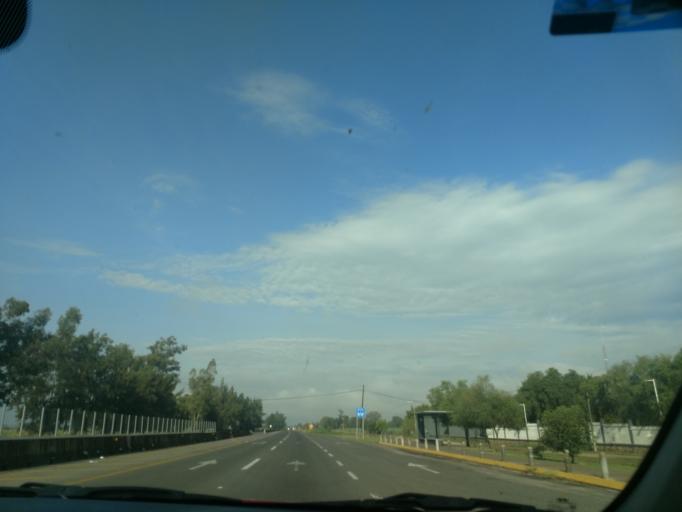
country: MX
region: Jalisco
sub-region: Ameca
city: Los Pocitos
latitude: 20.5342
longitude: -103.9674
